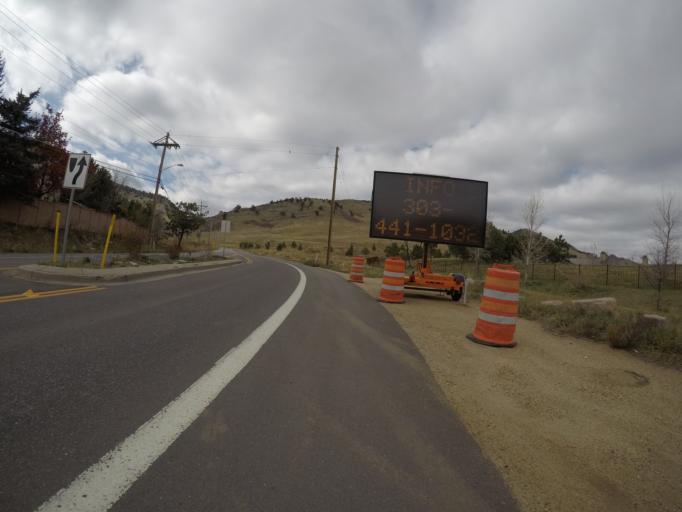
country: US
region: Colorado
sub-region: Boulder County
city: Boulder
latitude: 40.0640
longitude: -105.2908
